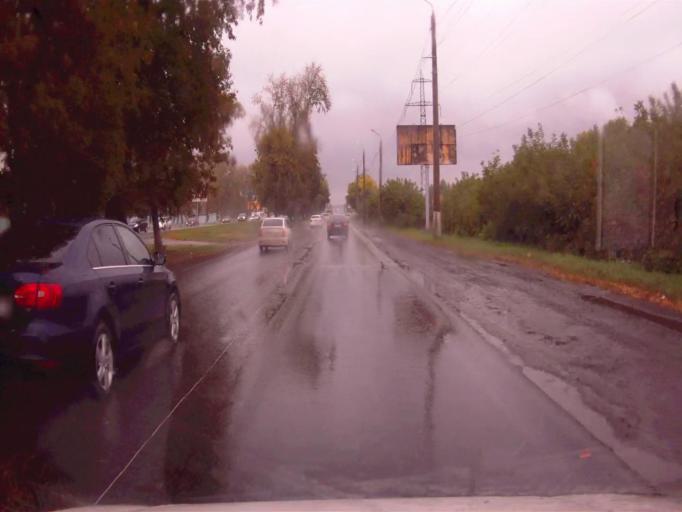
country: RU
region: Chelyabinsk
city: Dolgoderevenskoye
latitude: 55.2506
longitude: 61.3561
